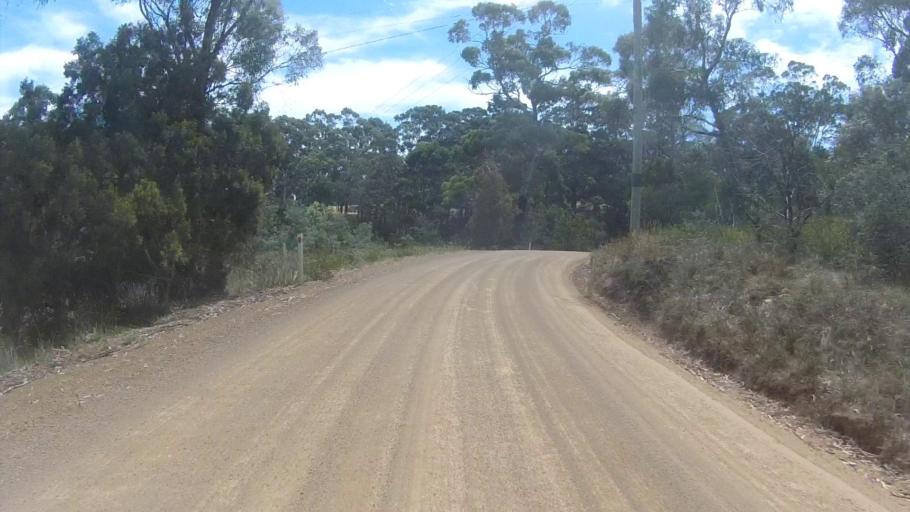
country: AU
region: Tasmania
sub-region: Kingborough
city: Blackmans Bay
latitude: -43.0472
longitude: 147.3076
